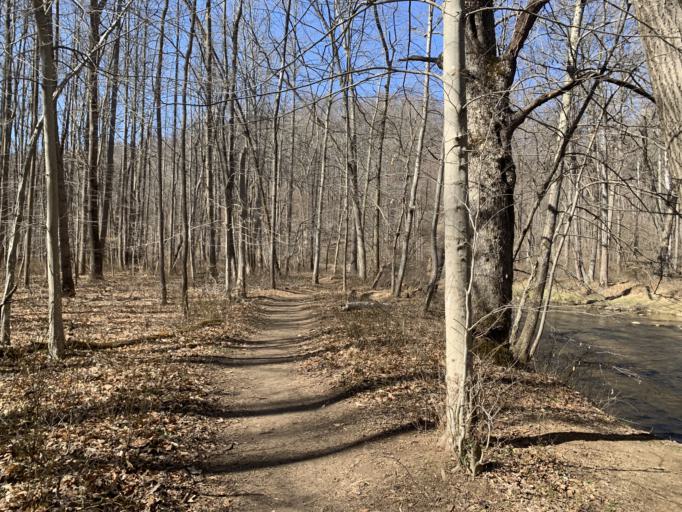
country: US
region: Maryland
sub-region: Harford County
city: Pleasant Hills
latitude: 39.4777
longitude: -76.4102
